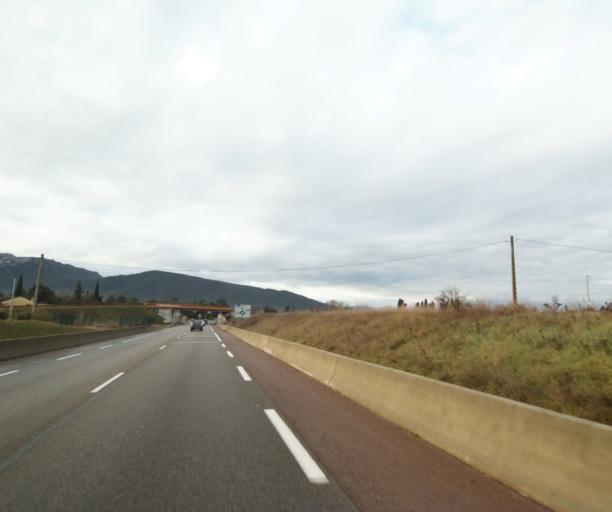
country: FR
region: Provence-Alpes-Cote d'Azur
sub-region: Departement du Var
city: La Celle
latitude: 43.4107
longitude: 6.0452
